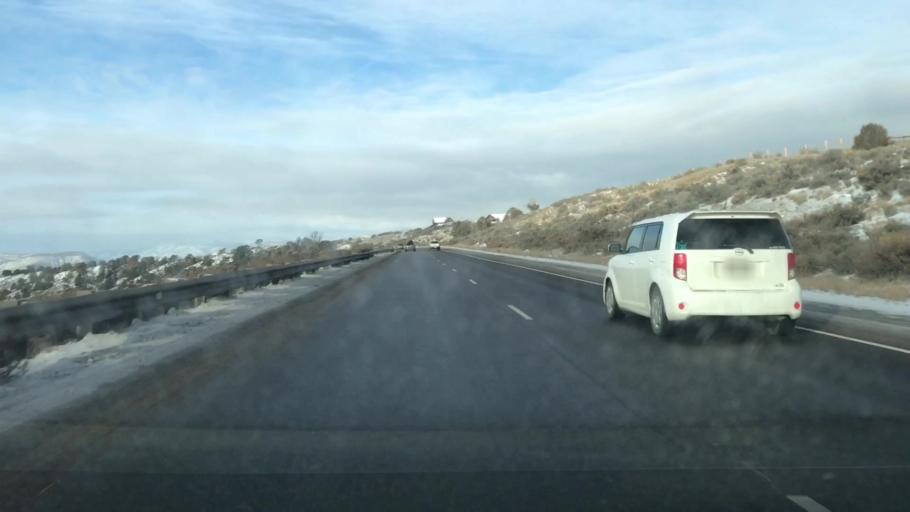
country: US
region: Colorado
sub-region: Eagle County
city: Eagle
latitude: 39.6545
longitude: -106.8420
